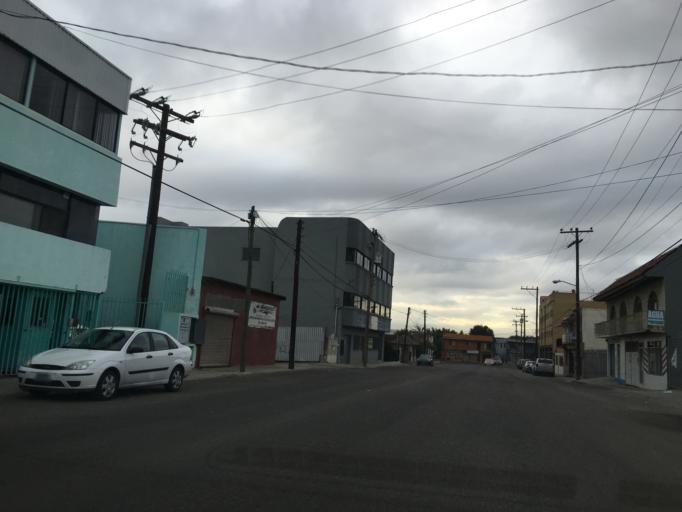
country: MX
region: Baja California
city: Tijuana
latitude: 32.5367
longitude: -117.0526
